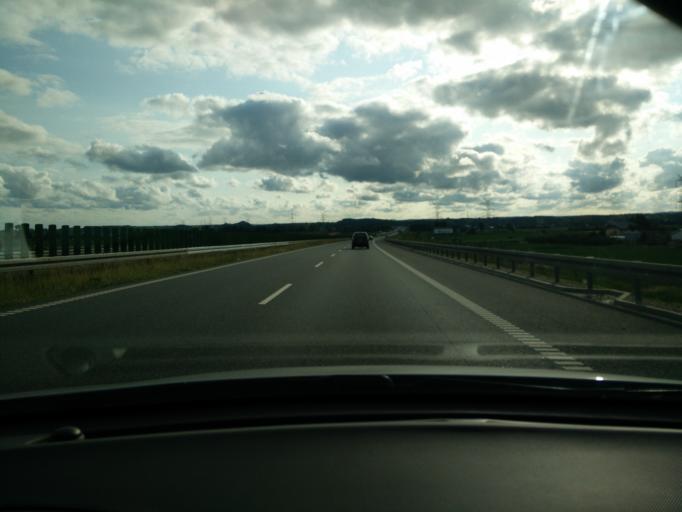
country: PL
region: Pomeranian Voivodeship
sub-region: Gdansk
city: Gdansk
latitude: 54.3128
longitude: 18.6803
